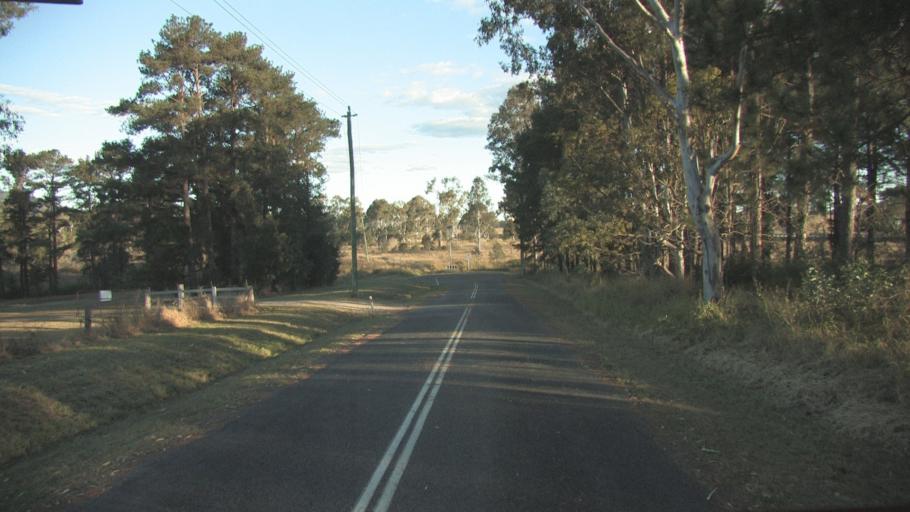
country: AU
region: Queensland
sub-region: Logan
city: Cedar Vale
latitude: -27.8625
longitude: 153.1222
